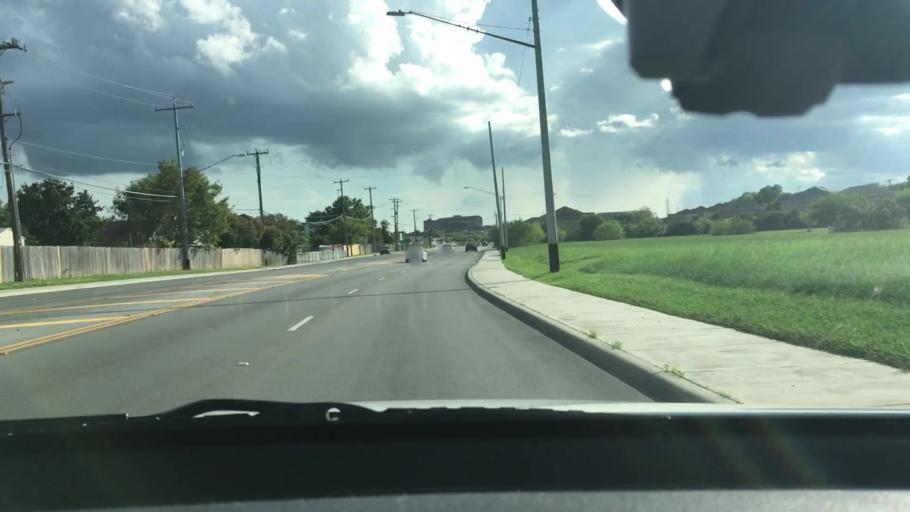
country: US
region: Texas
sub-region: Bexar County
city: Converse
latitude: 29.5309
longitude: -98.3363
